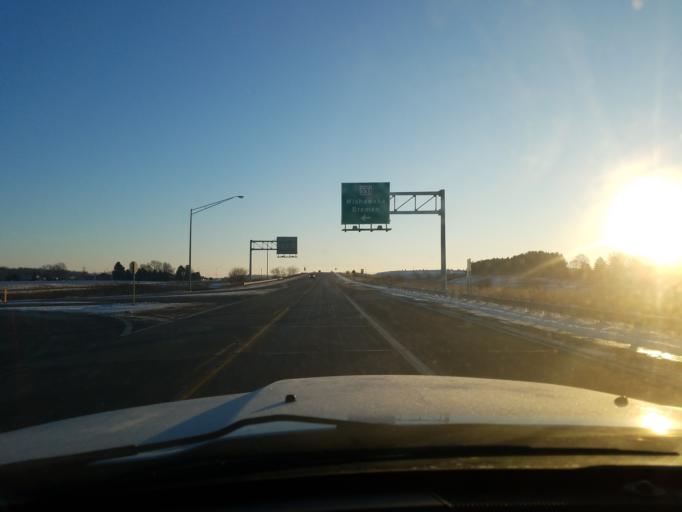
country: US
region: Indiana
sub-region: Marshall County
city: Bremen
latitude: 41.4607
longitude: -86.1621
